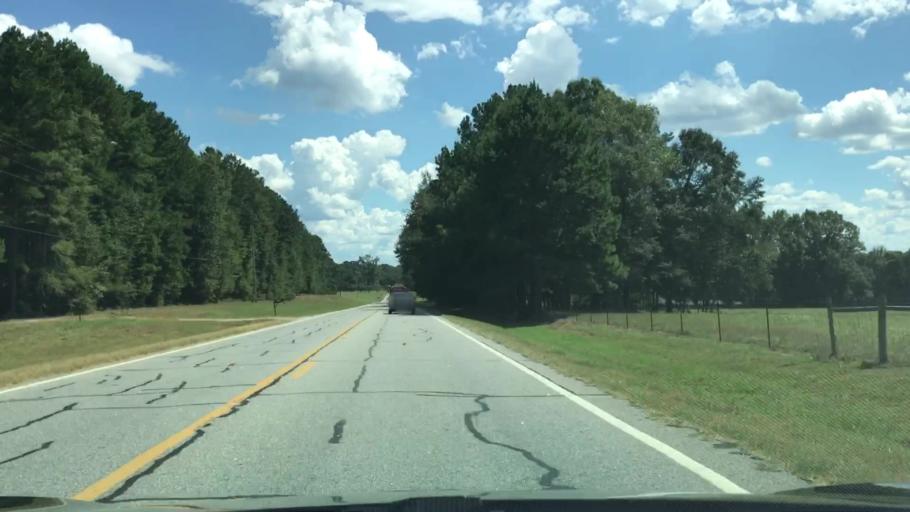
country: US
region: Georgia
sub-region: Oconee County
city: Watkinsville
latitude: 33.7563
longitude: -83.3056
